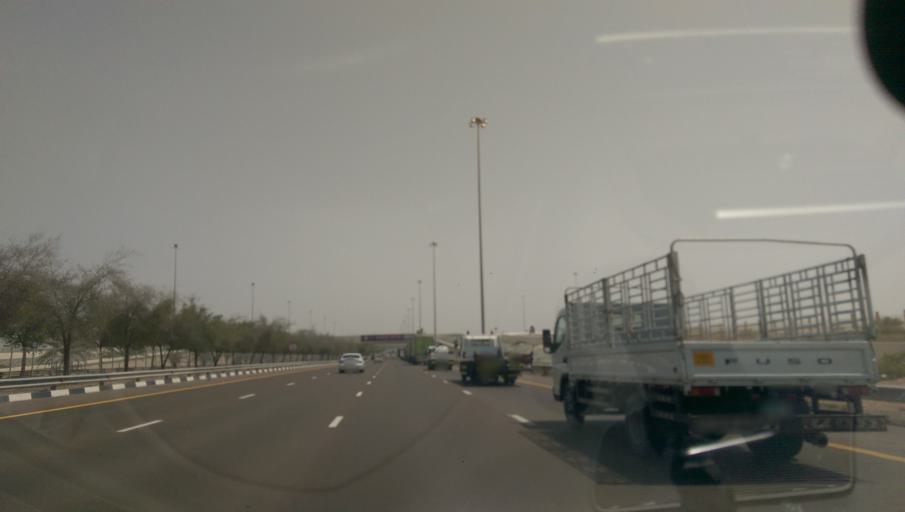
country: AE
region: Abu Dhabi
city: Abu Dhabi
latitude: 24.5601
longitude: 54.6956
